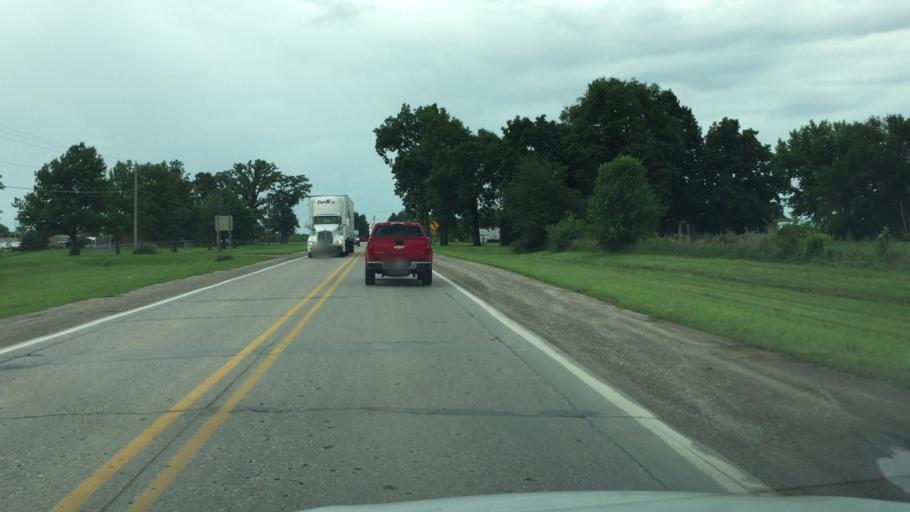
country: US
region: Iowa
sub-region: Jasper County
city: Newton
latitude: 41.7178
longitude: -93.0579
